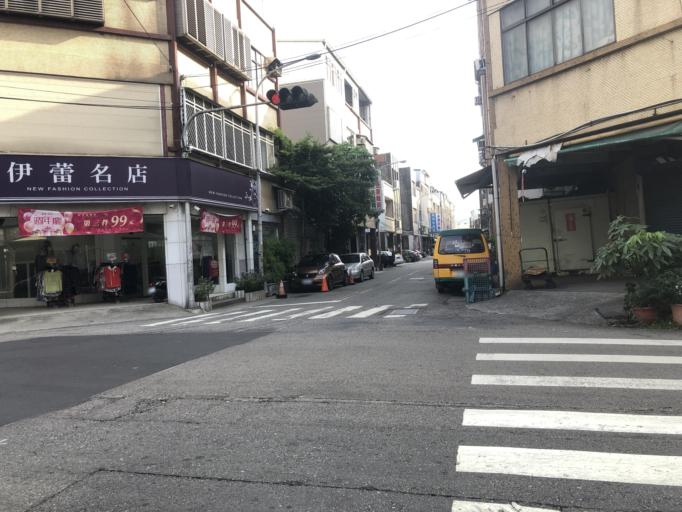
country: TW
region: Taiwan
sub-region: Miaoli
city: Miaoli
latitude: 24.4863
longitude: 120.7881
